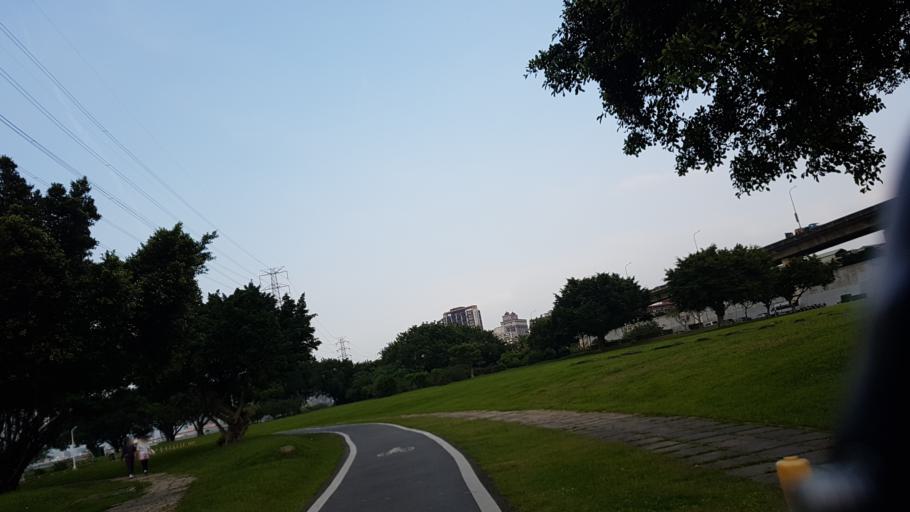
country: TW
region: Taipei
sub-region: Taipei
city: Banqiao
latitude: 25.0367
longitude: 121.4898
